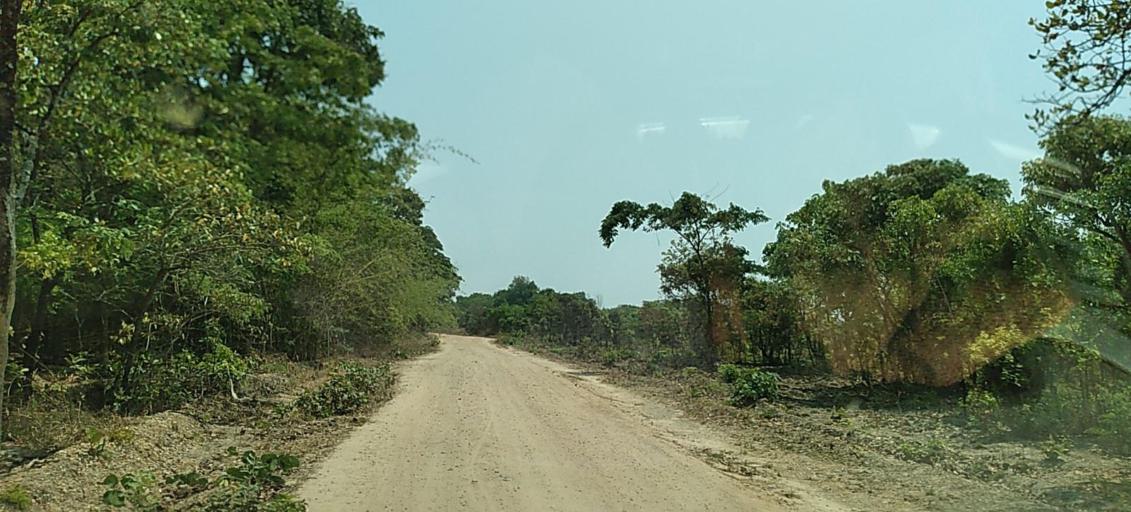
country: ZM
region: Copperbelt
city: Kalulushi
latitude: -12.9450
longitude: 28.1532
